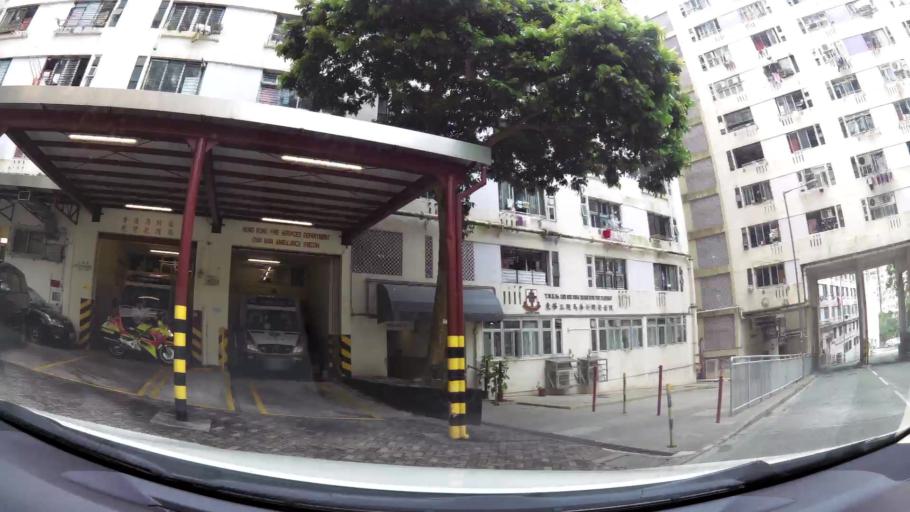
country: HK
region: Wanchai
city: Wan Chai
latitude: 22.2625
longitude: 114.2332
